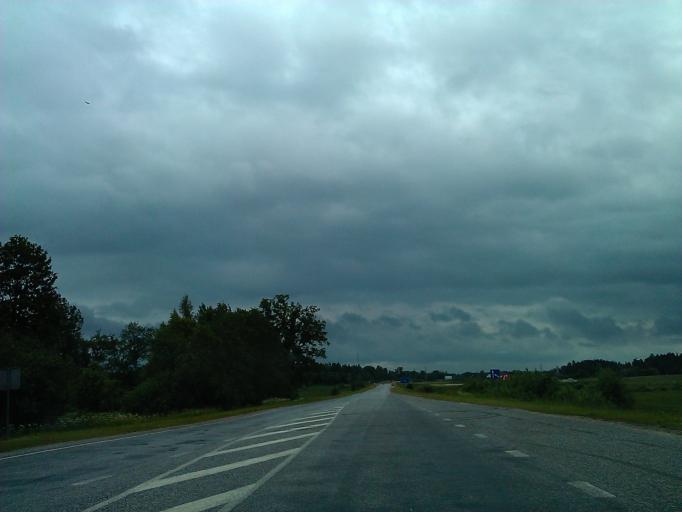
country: LV
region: Kuldigas Rajons
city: Kuldiga
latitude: 56.9785
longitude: 22.0164
